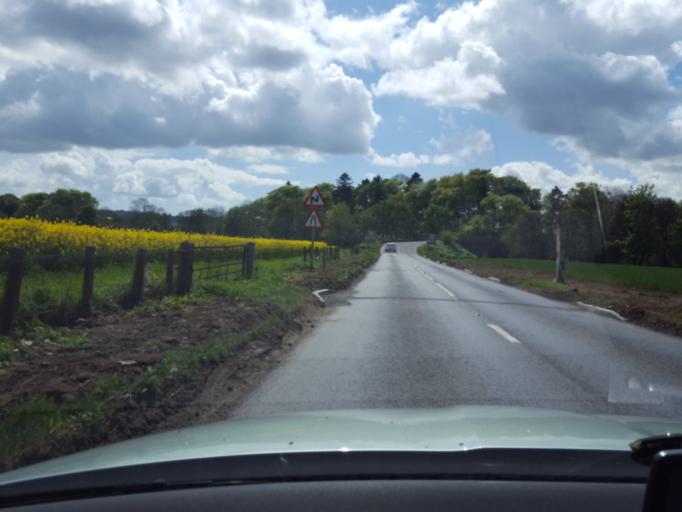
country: GB
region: Scotland
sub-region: Angus
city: Brechin
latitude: 56.7853
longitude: -2.6456
